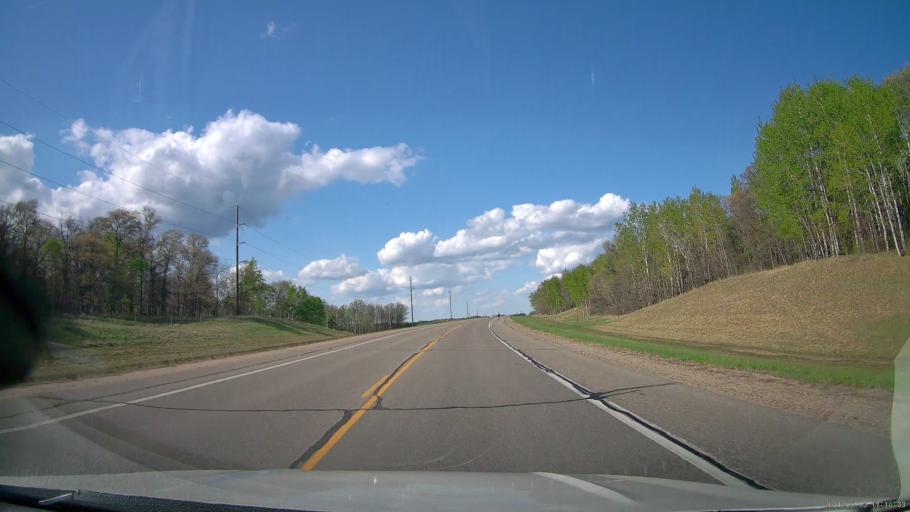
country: US
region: Minnesota
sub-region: Hubbard County
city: Park Rapids
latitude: 46.9631
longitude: -95.0180
